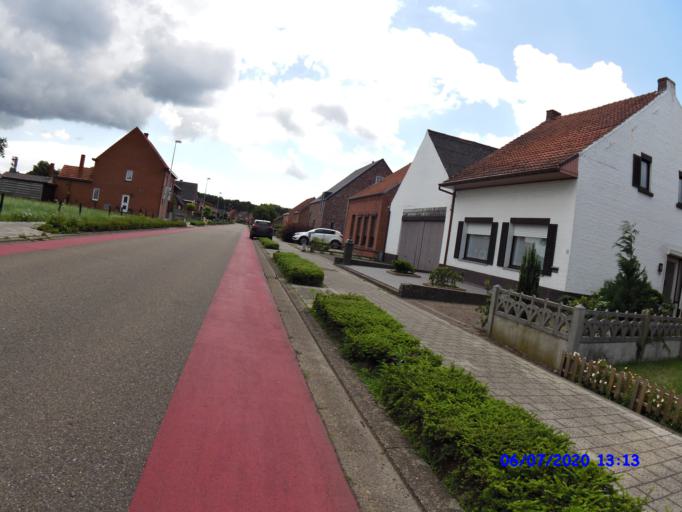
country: BE
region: Flanders
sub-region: Provincie Antwerpen
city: Dessel
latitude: 51.2383
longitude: 5.1571
